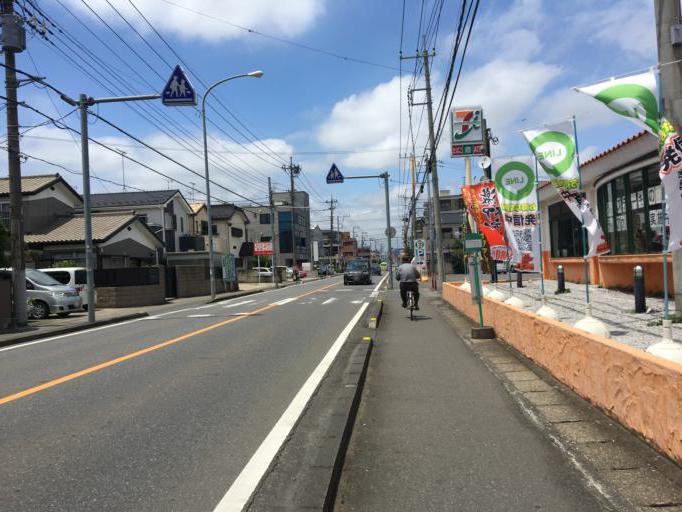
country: JP
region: Saitama
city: Okegawa
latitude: 35.9826
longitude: 139.5818
